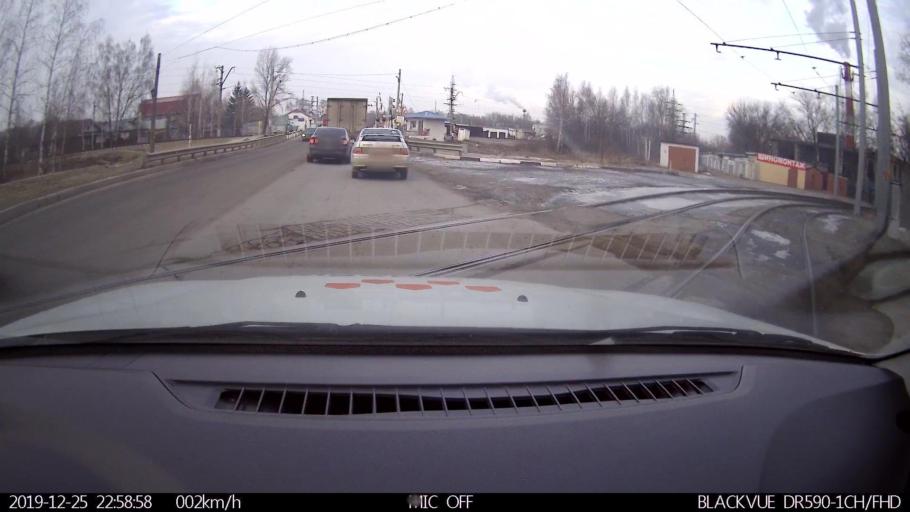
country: RU
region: Nizjnij Novgorod
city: Gorbatovka
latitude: 56.3472
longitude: 43.8382
